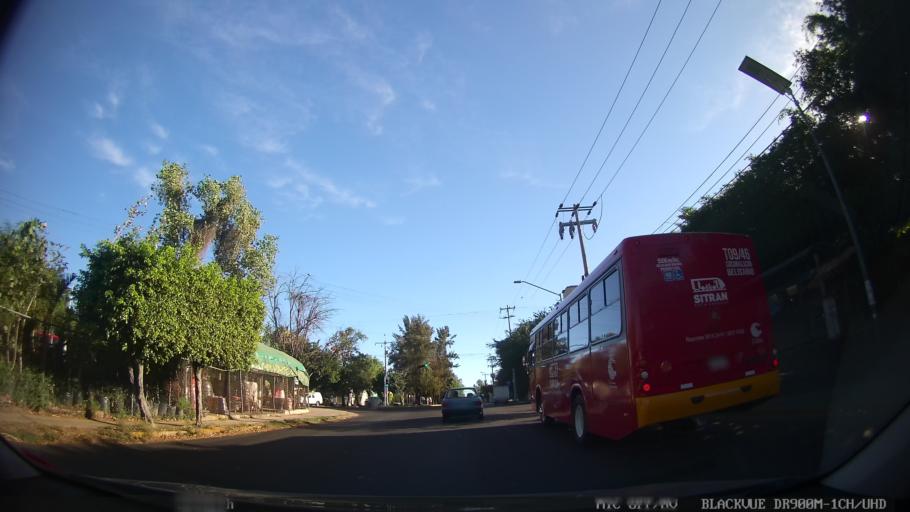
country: MX
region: Jalisco
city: Tlaquepaque
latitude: 20.6826
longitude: -103.2947
